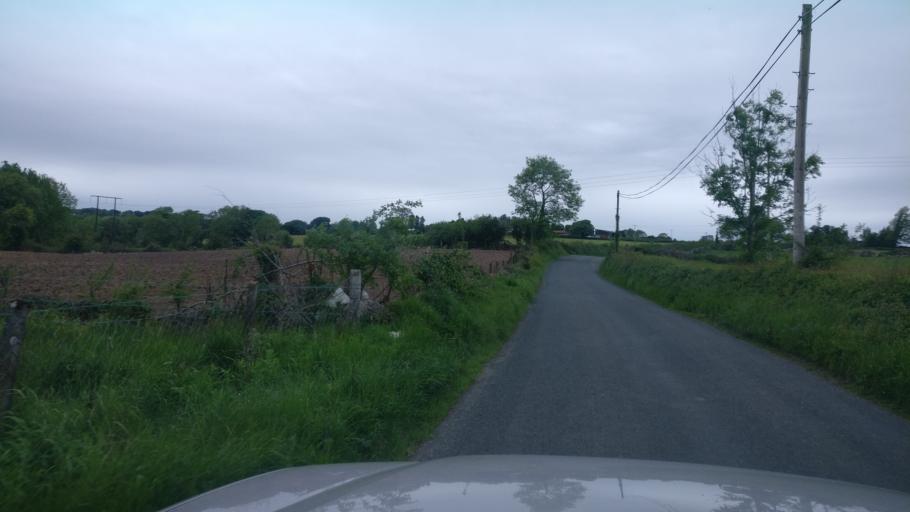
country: IE
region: Connaught
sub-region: County Galway
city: Loughrea
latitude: 53.1188
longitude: -8.4268
